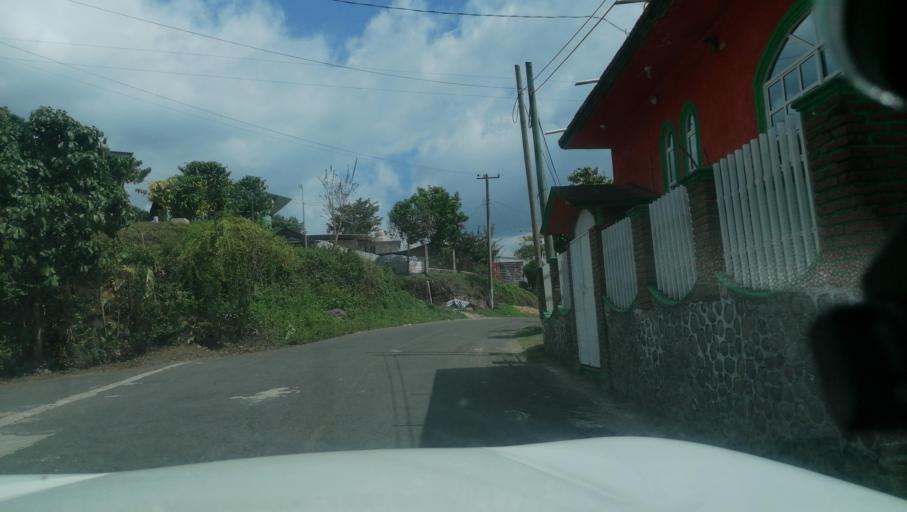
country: MX
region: Chiapas
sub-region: Cacahoatan
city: Benito Juarez
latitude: 15.0443
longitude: -92.1520
